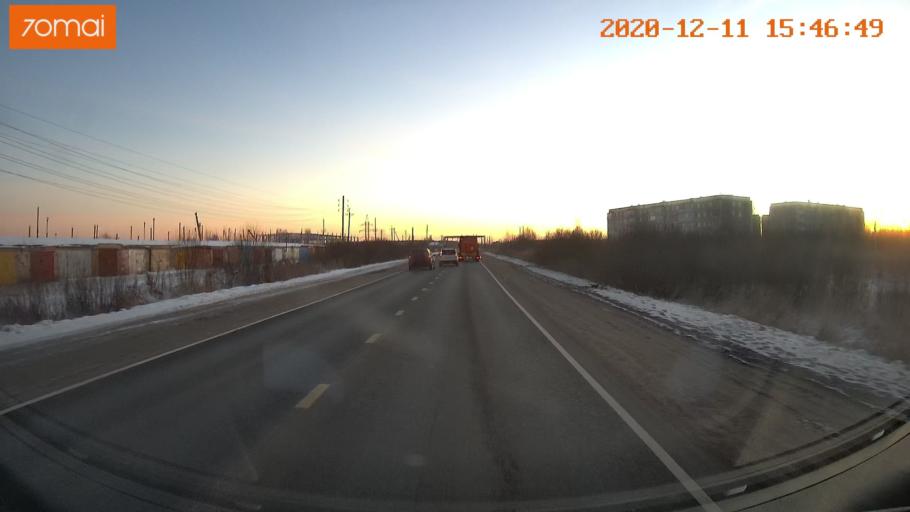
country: RU
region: Ivanovo
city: Novo-Talitsy
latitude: 57.0032
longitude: 40.8551
